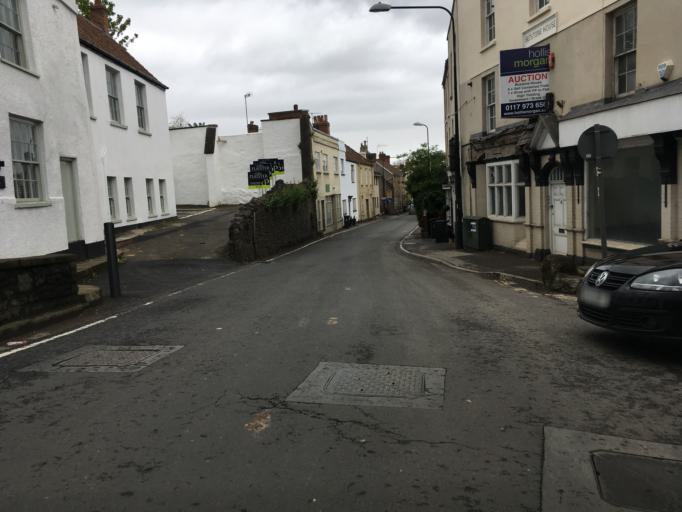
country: GB
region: England
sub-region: North Somerset
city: Banwell
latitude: 51.3275
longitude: -2.8643
